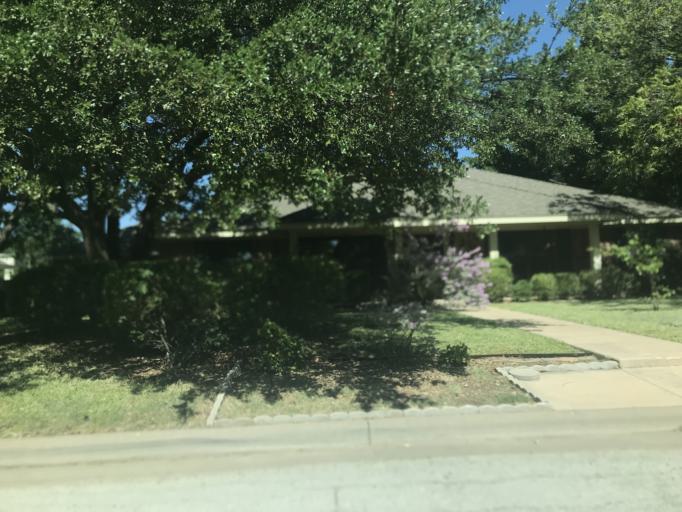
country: US
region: Texas
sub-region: Taylor County
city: Abilene
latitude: 32.4223
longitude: -99.7005
